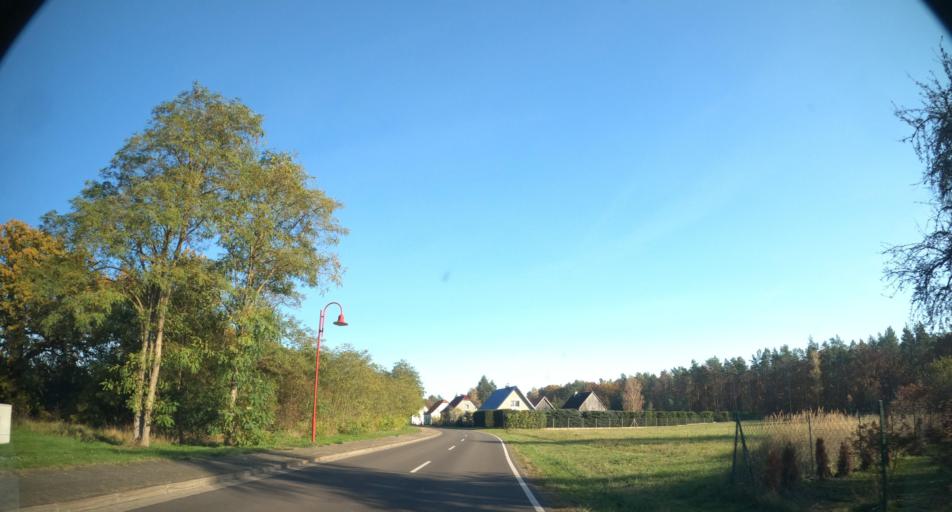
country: DE
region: Mecklenburg-Vorpommern
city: Ahlbeck
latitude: 53.6194
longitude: 14.2581
